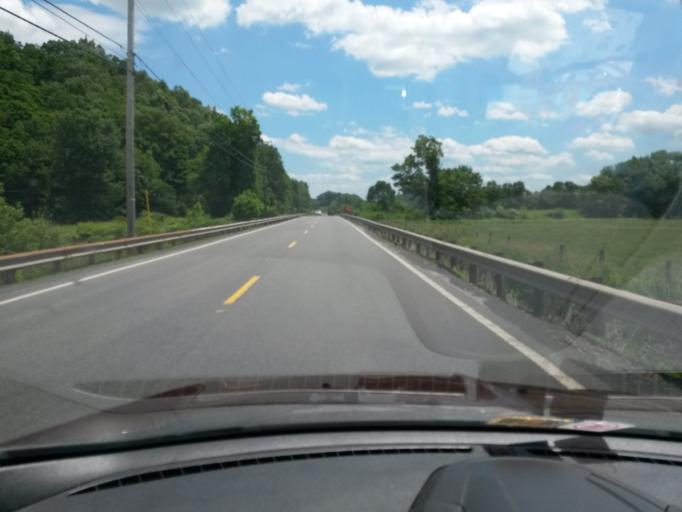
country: US
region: West Virginia
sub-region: Greenbrier County
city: Rainelle
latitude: 37.9499
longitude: -80.6562
